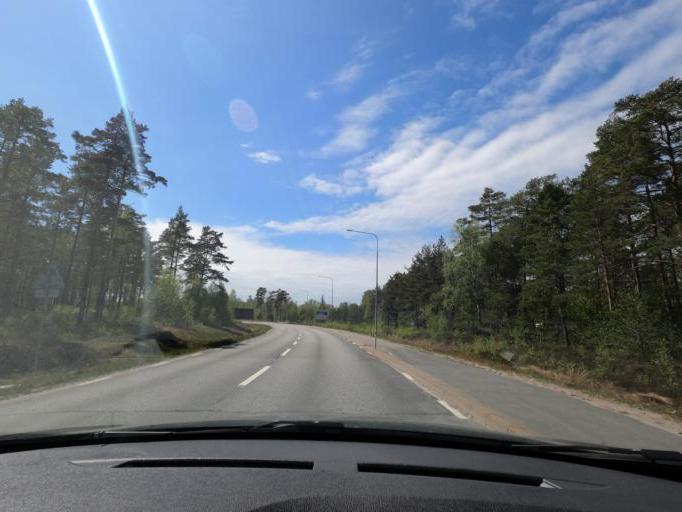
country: SE
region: Joenkoeping
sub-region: Varnamo Kommun
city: Bredaryd
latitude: 57.1785
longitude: 13.7436
